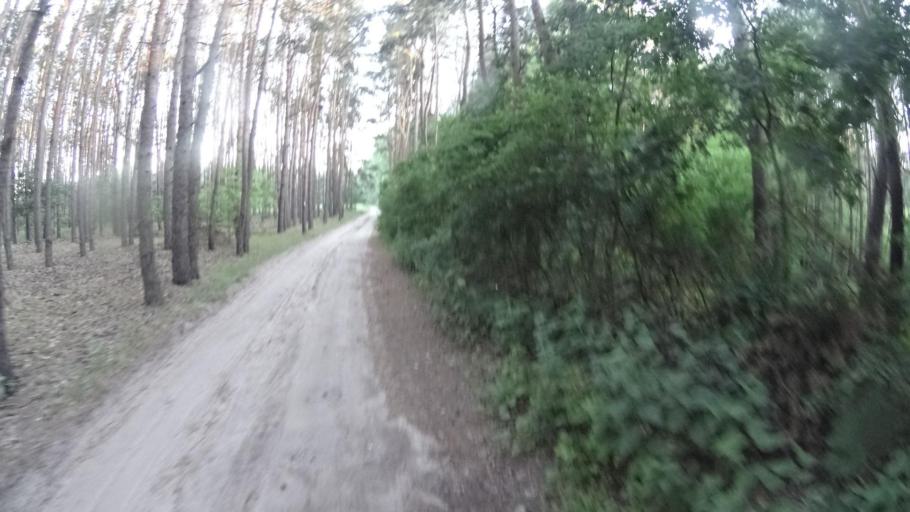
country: PL
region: Masovian Voivodeship
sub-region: Powiat warszawski zachodni
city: Jozefow
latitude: 52.2717
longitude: 20.6957
